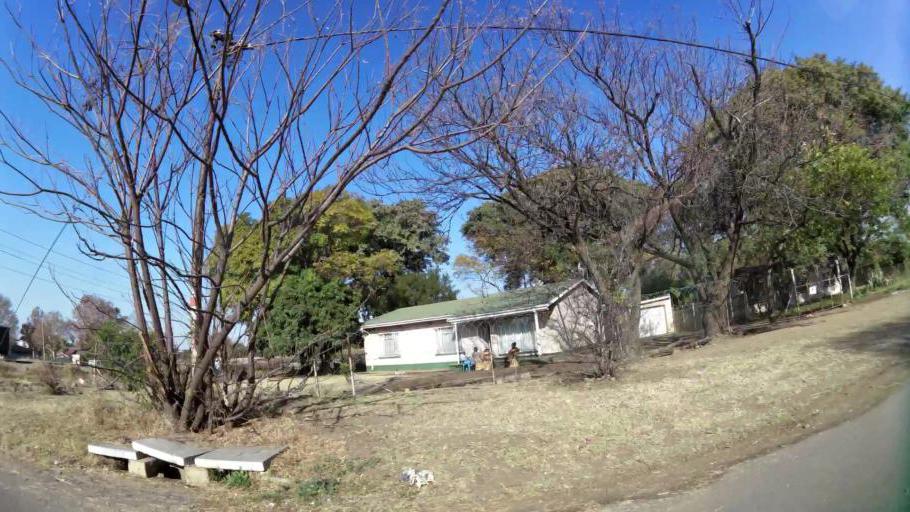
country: ZA
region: North-West
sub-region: Bojanala Platinum District Municipality
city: Rustenburg
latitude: -25.6517
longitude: 27.2399
